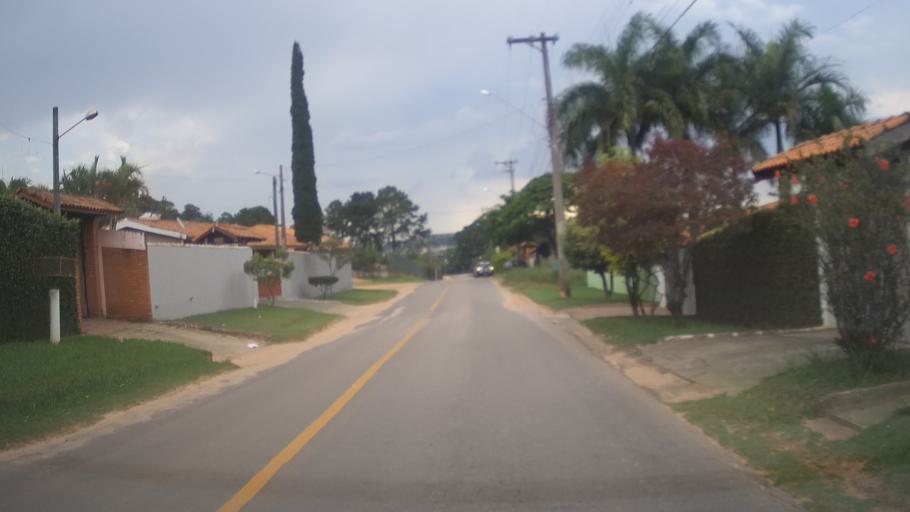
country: BR
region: Sao Paulo
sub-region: Itupeva
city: Itupeva
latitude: -23.1675
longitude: -47.0776
